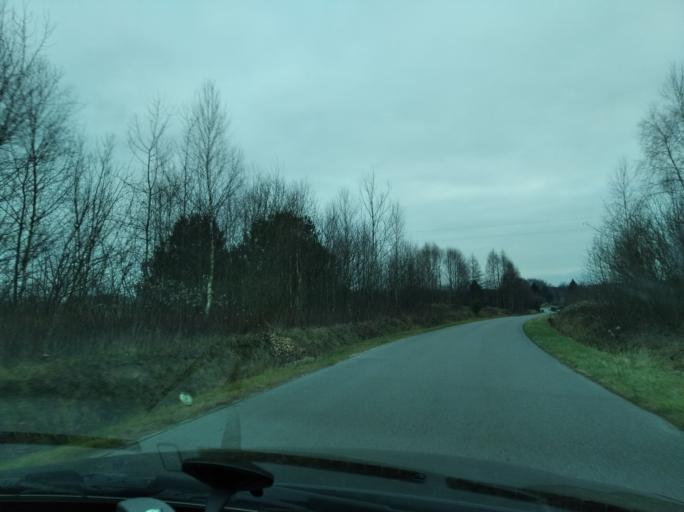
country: PL
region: Subcarpathian Voivodeship
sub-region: Powiat lancucki
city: Brzoza Stadnicka
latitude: 50.2013
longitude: 22.2801
